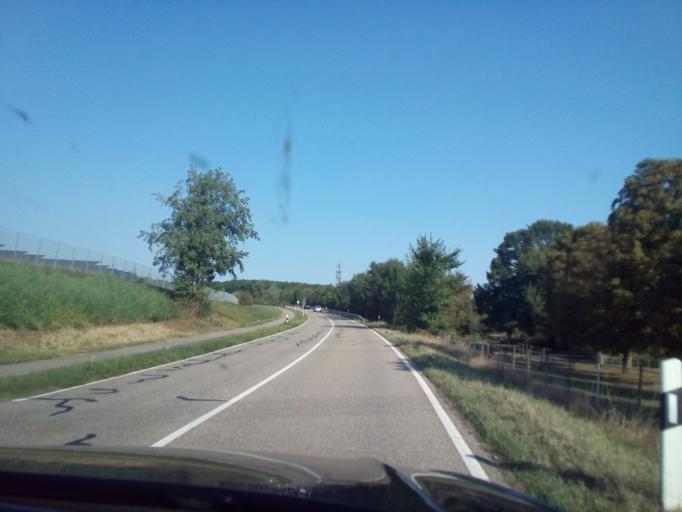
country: DE
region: Baden-Wuerttemberg
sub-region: Karlsruhe Region
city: Sinzheim
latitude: 48.7808
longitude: 8.1520
